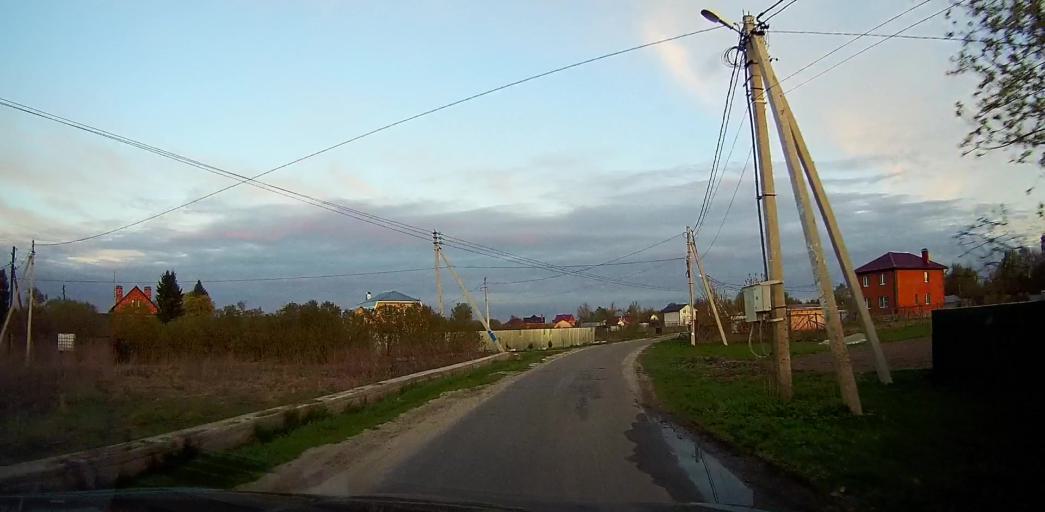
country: RU
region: Moskovskaya
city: Peski
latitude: 55.2114
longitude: 38.7401
